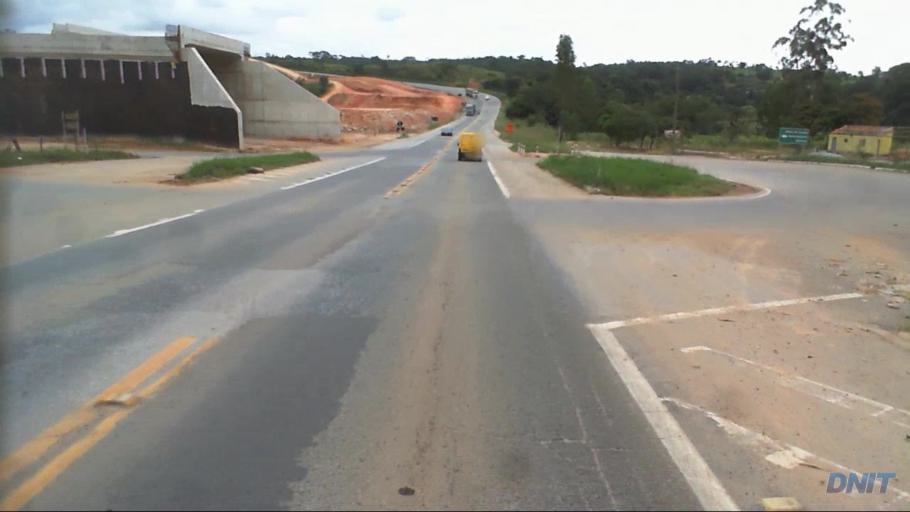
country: BR
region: Minas Gerais
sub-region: Barao De Cocais
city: Barao de Cocais
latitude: -19.7889
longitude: -43.4295
